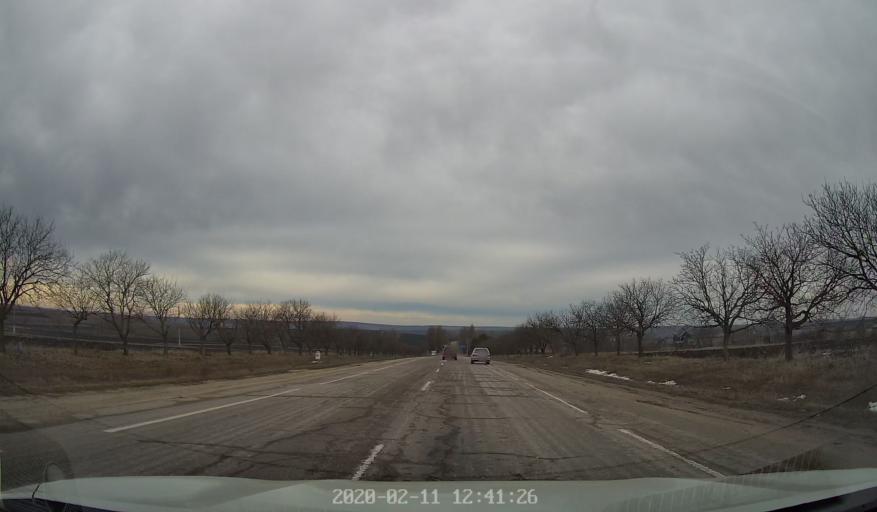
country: MD
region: Raionul Edinet
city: Edinet
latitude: 48.2148
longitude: 27.2405
